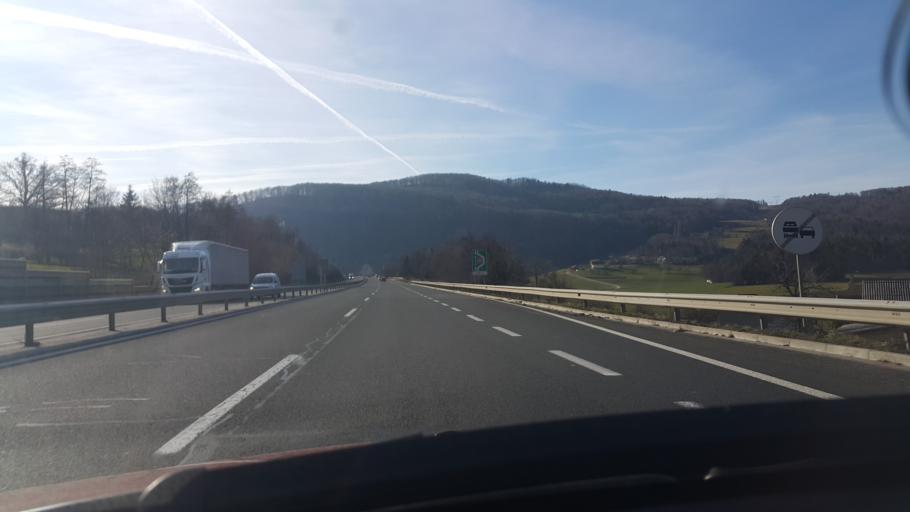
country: SI
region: Slovenska Konjice
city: Slovenske Konjice
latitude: 46.3266
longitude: 15.4652
